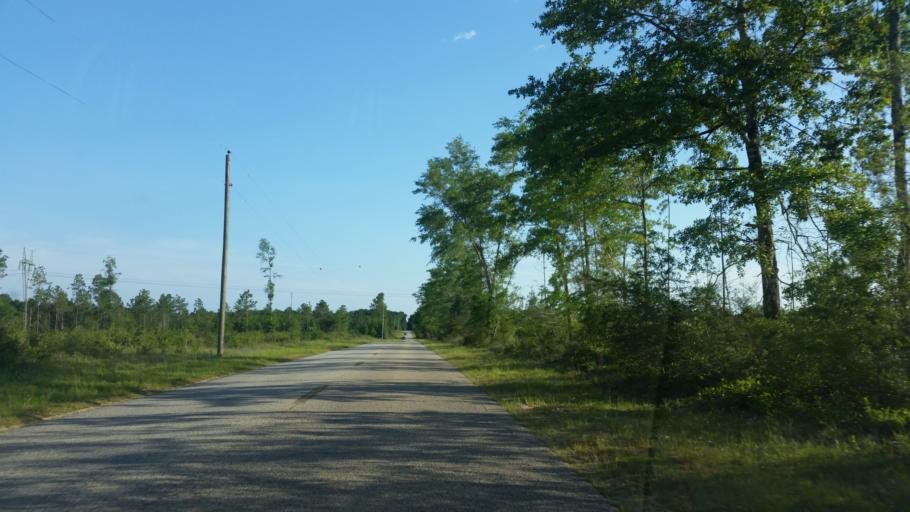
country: US
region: Florida
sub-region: Santa Rosa County
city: East Milton
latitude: 30.6693
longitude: -86.8777
